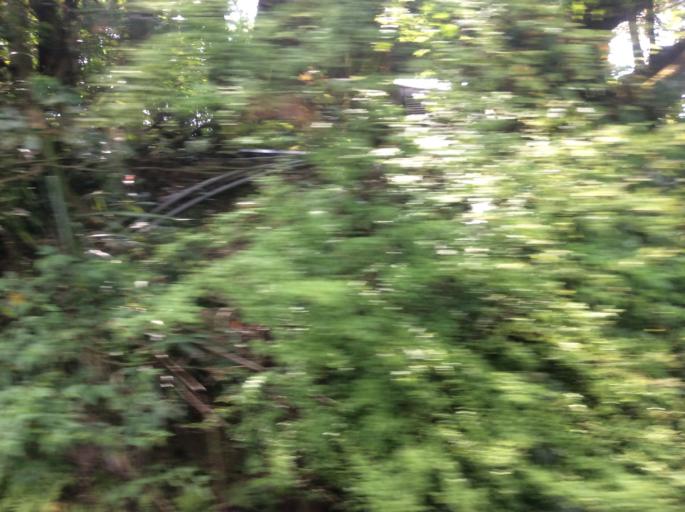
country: TW
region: Taipei
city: Taipei
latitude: 25.1623
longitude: 121.5441
